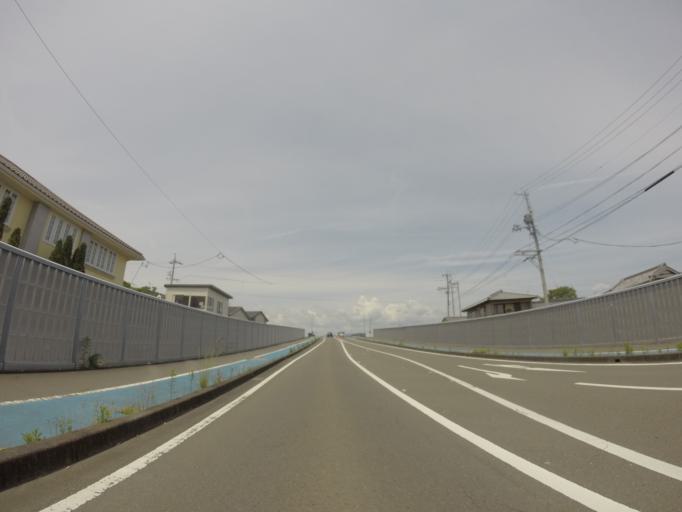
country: JP
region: Shizuoka
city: Fujieda
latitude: 34.8660
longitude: 138.2829
